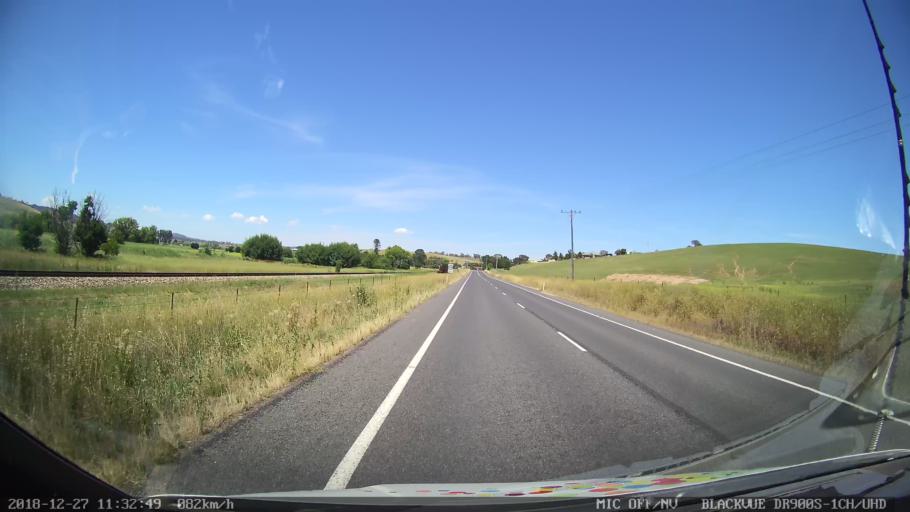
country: AU
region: New South Wales
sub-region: Bathurst Regional
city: Perthville
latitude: -33.5105
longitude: 149.5294
